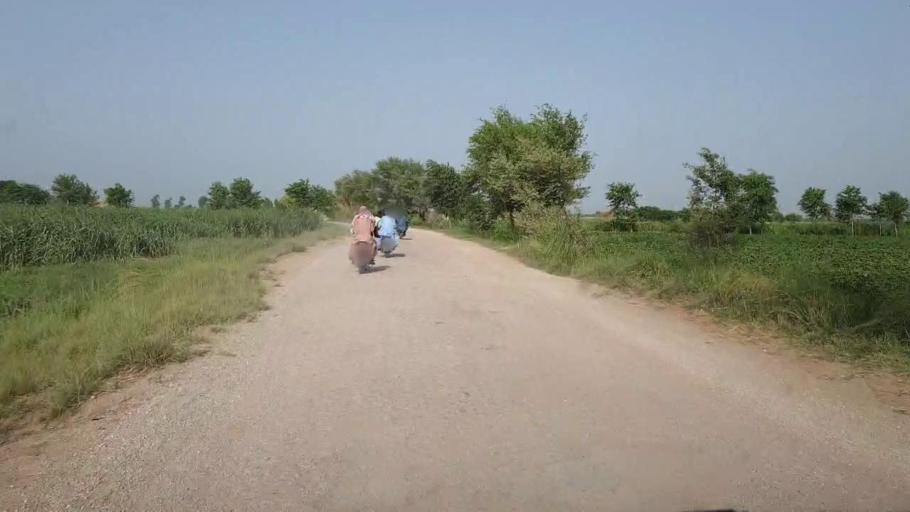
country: PK
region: Sindh
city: Daur
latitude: 26.3481
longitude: 68.1702
